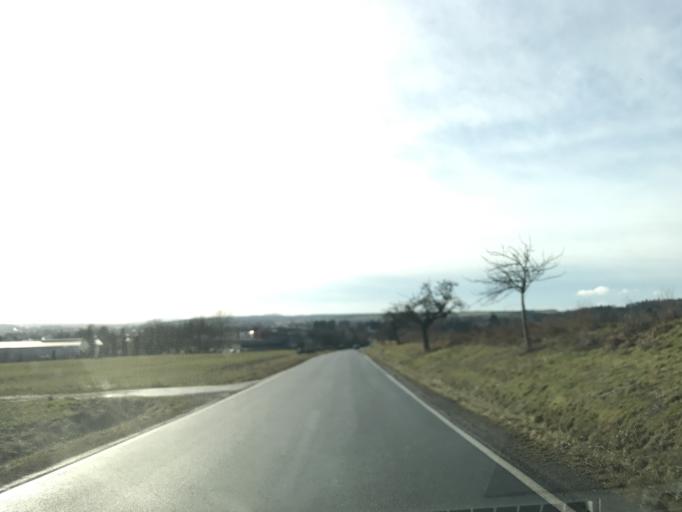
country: DE
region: Hesse
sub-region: Regierungsbezirk Kassel
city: Hofgeismar
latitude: 51.5100
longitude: 9.3880
